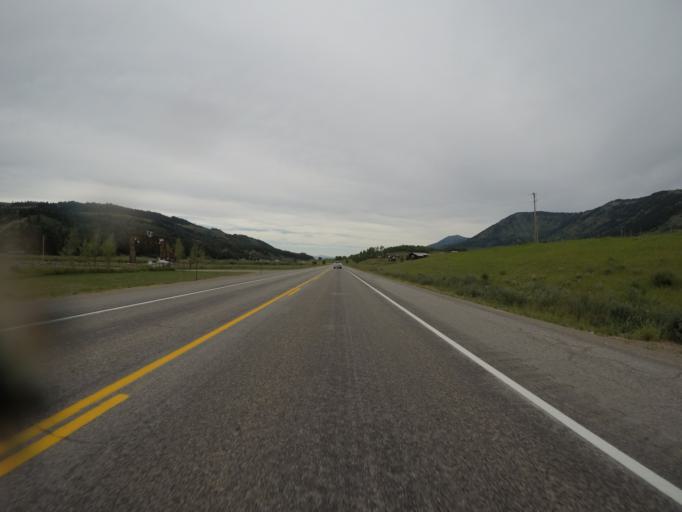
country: US
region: Wyoming
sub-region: Lincoln County
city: Afton
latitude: 42.5588
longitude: -110.8953
